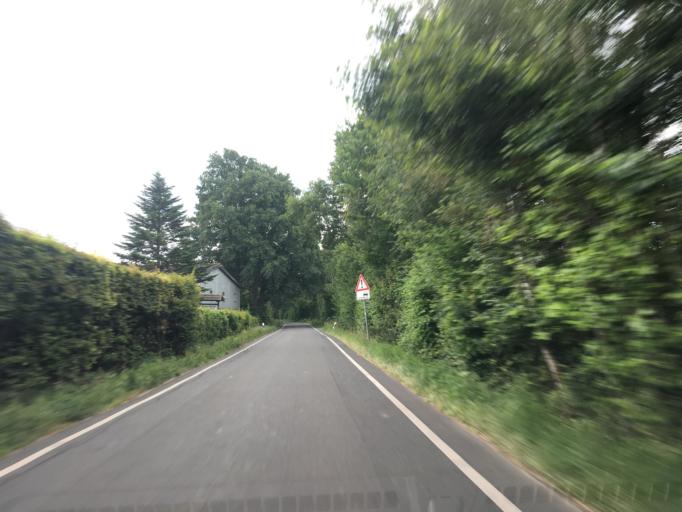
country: DE
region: North Rhine-Westphalia
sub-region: Regierungsbezirk Munster
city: Telgte
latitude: 51.9586
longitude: 7.7134
